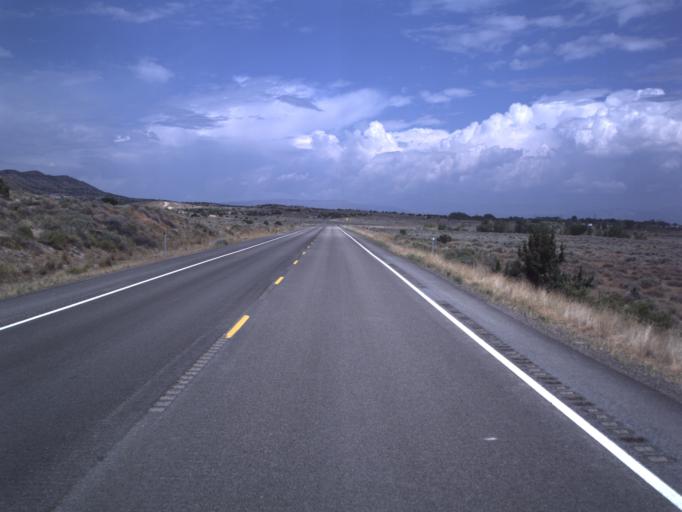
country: US
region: Utah
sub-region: Uintah County
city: Naples
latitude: 40.3511
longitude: -109.4920
